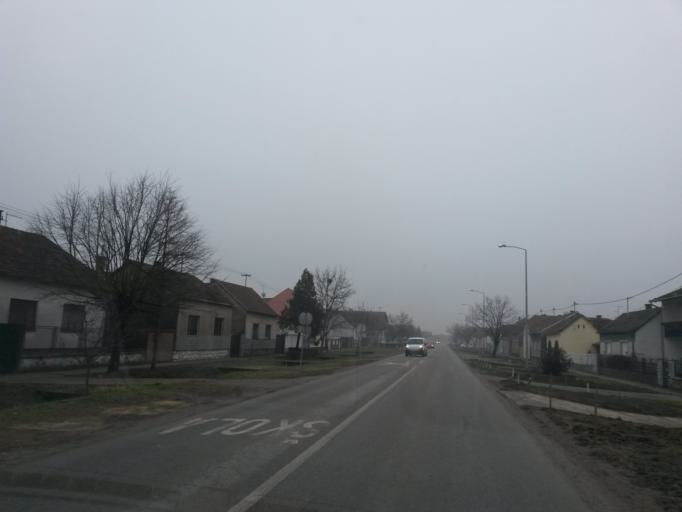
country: HR
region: Vukovarsko-Srijemska
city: Zupanja
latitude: 45.0875
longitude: 18.6991
